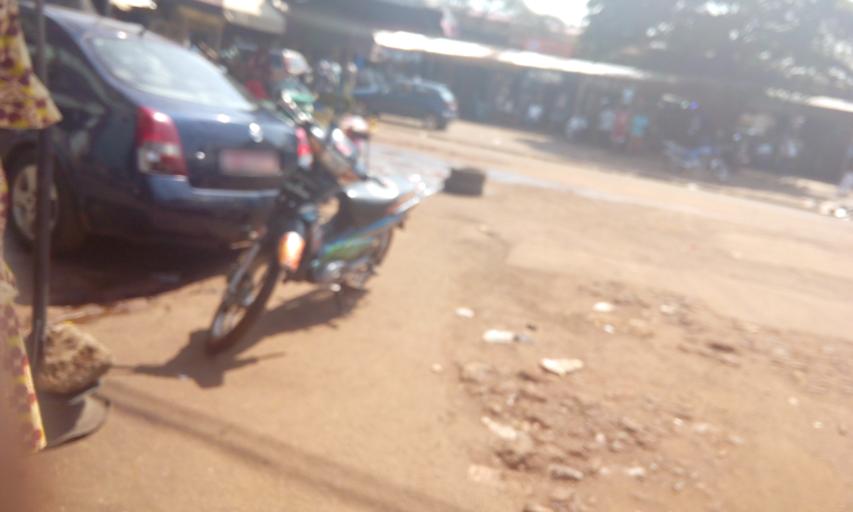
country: GN
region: Conakry
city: Conakry
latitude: 9.5482
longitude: -13.6742
